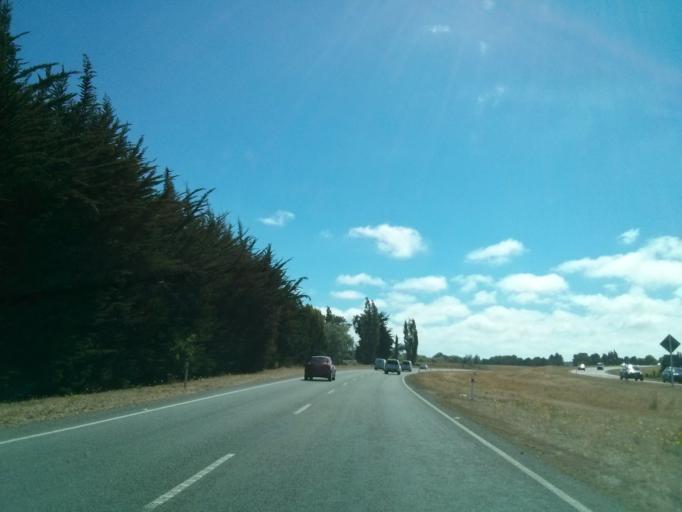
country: NZ
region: Canterbury
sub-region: Waimakariri District
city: Kaiapoi
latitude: -43.4336
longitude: 172.6401
